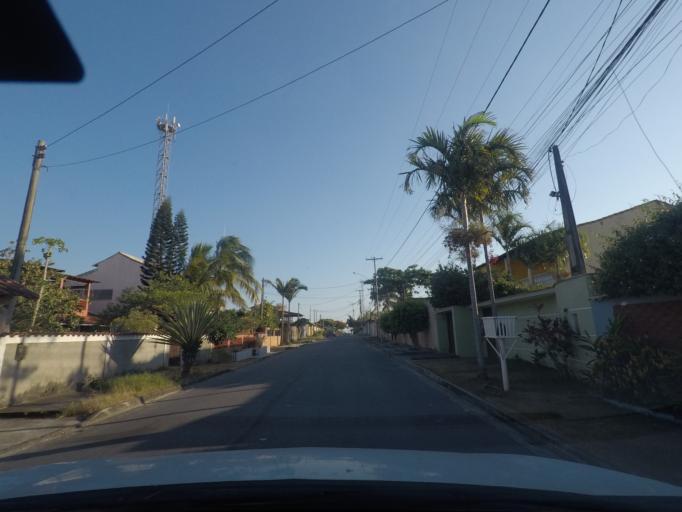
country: BR
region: Rio de Janeiro
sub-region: Marica
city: Marica
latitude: -22.9674
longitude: -42.9343
